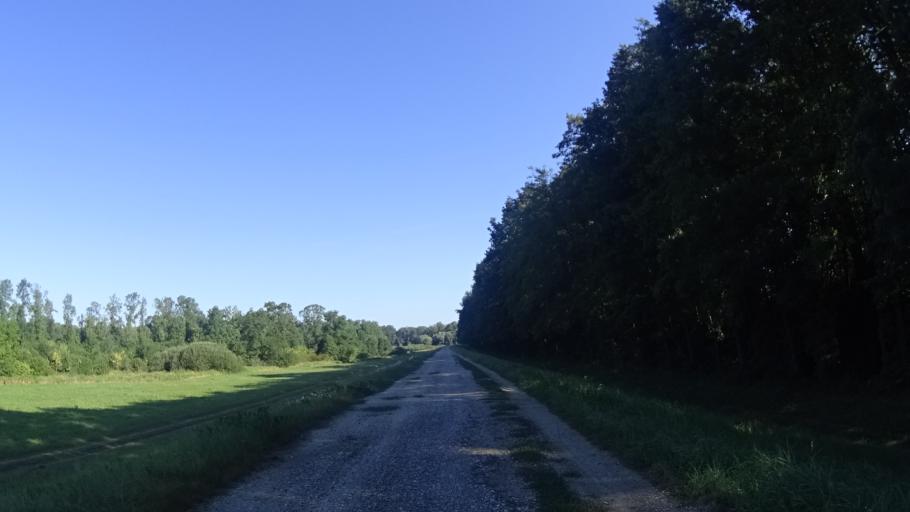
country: CZ
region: South Moravian
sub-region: Okres Breclav
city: Lanzhot
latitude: 48.6490
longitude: 16.9769
